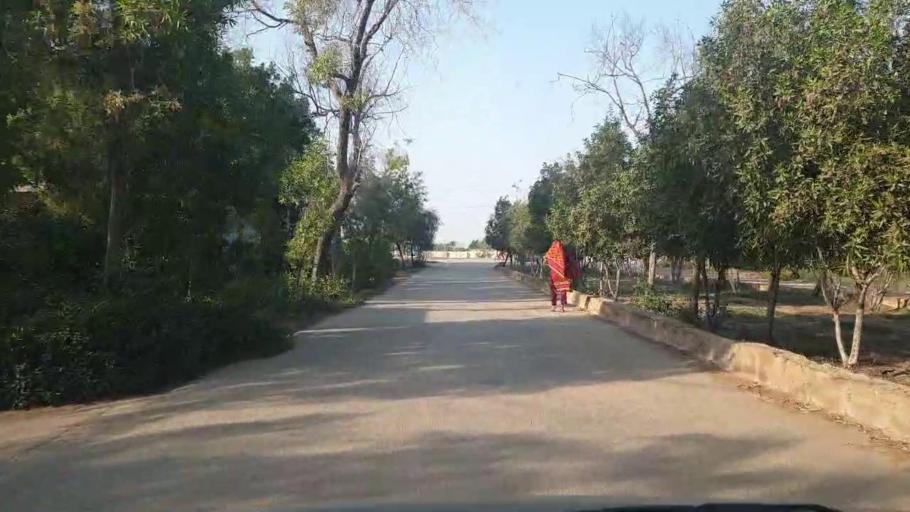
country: PK
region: Sindh
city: Badin
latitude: 24.6552
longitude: 68.8271
